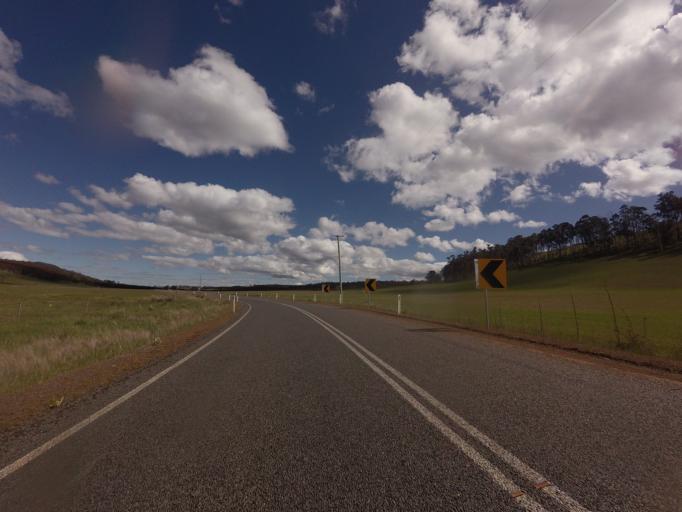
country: AU
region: Tasmania
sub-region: Brighton
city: Bridgewater
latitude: -42.4476
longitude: 147.3113
